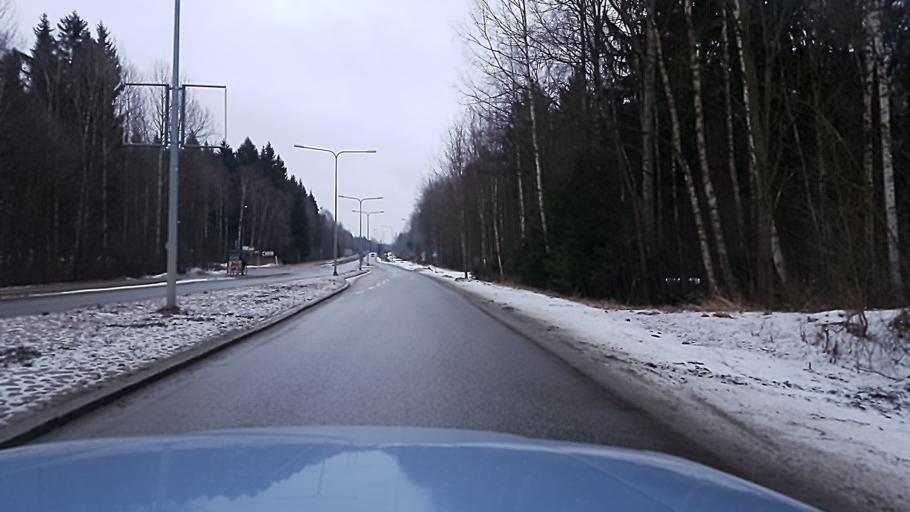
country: FI
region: Uusimaa
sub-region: Helsinki
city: Vantaa
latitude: 60.2637
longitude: 25.0552
